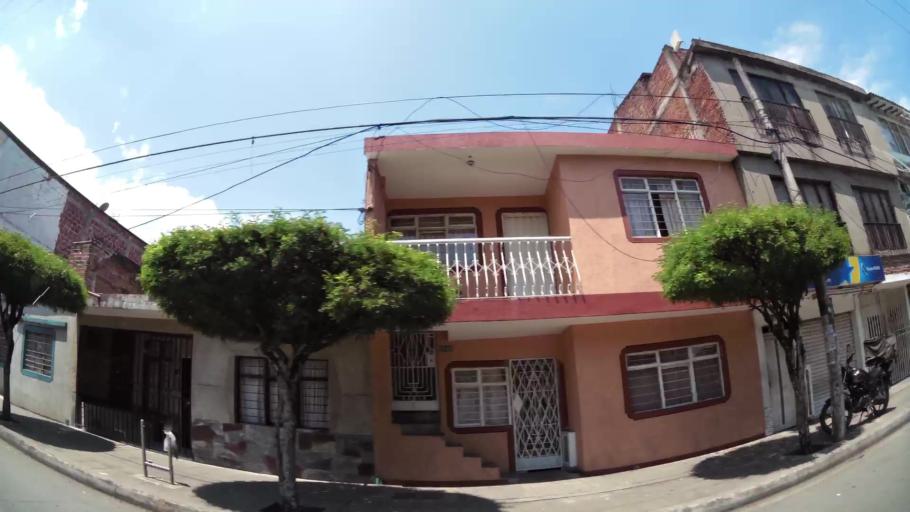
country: CO
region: Valle del Cauca
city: Cali
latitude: 3.4439
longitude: -76.4983
